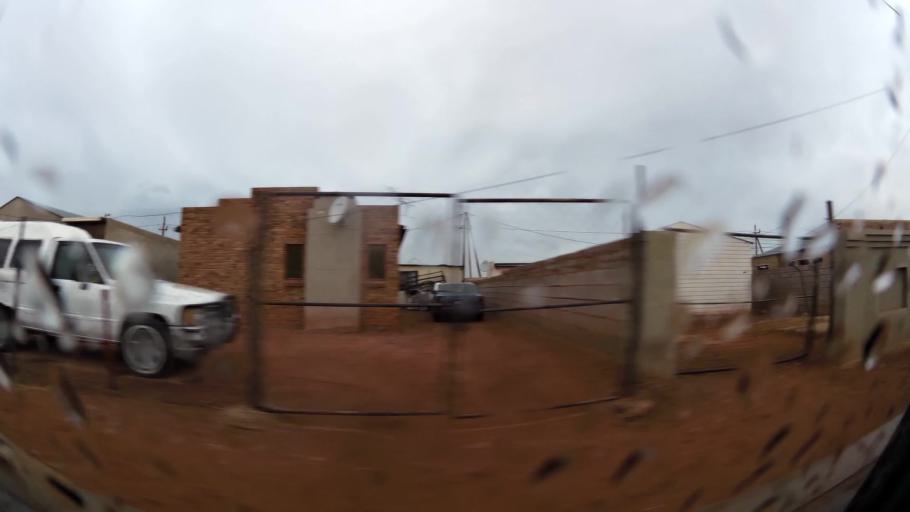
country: ZA
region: Gauteng
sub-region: West Rand District Municipality
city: Randfontein
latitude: -26.1761
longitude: 27.7800
